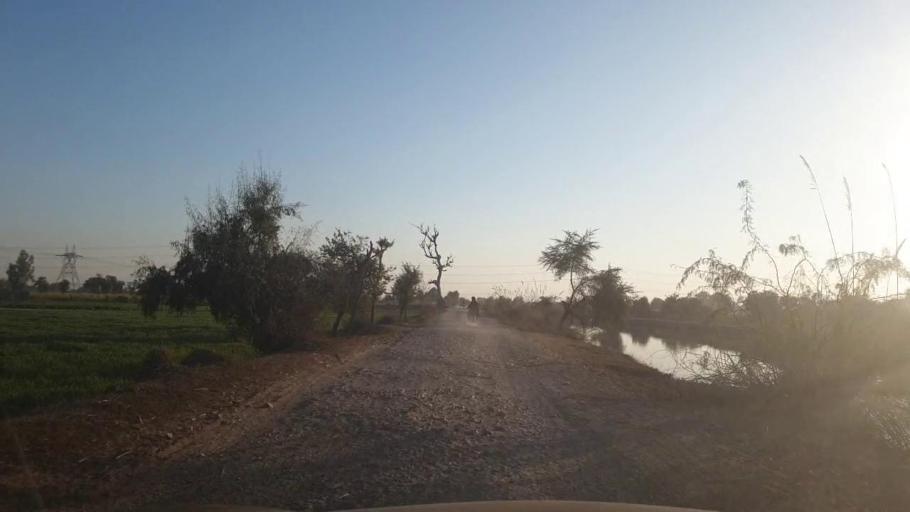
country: PK
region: Sindh
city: Mirpur Mathelo
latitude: 27.9926
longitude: 69.4657
